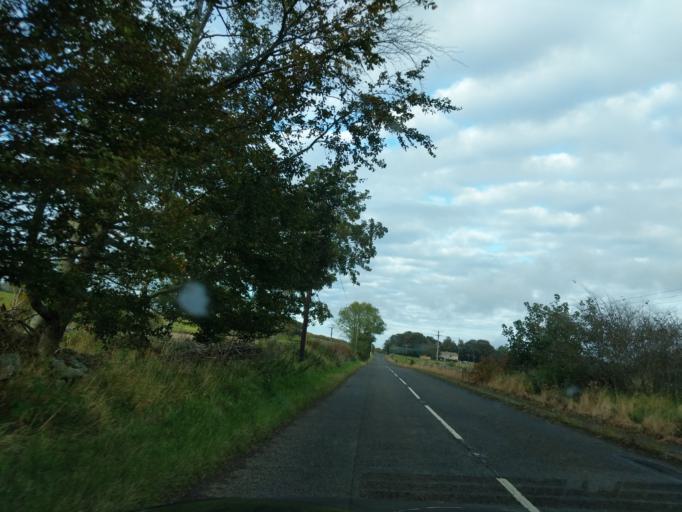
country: GB
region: Scotland
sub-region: Midlothian
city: Penicuik
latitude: 55.8218
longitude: -3.2672
